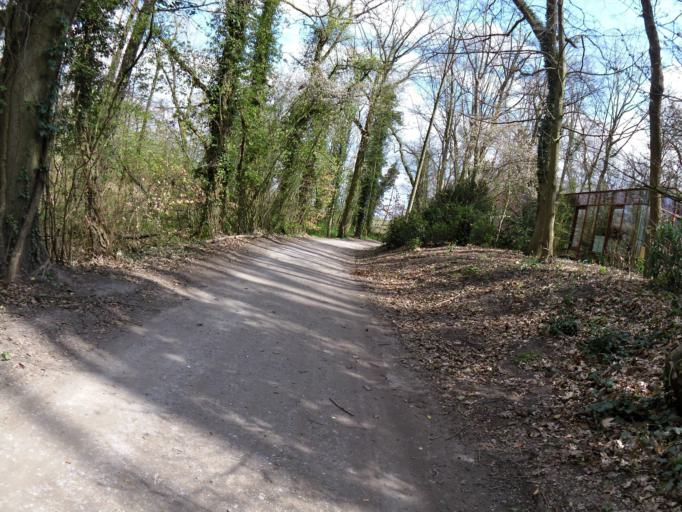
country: BE
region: Flanders
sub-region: Provincie Oost-Vlaanderen
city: Sint-Martens-Latem
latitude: 51.0258
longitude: 3.6297
